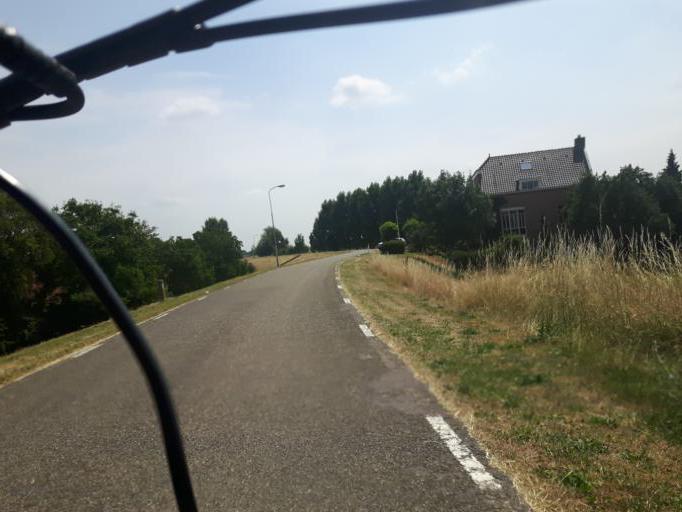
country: NL
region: North Brabant
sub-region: Gemeente Aalburg
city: Aalburg
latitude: 51.8196
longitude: 5.1243
